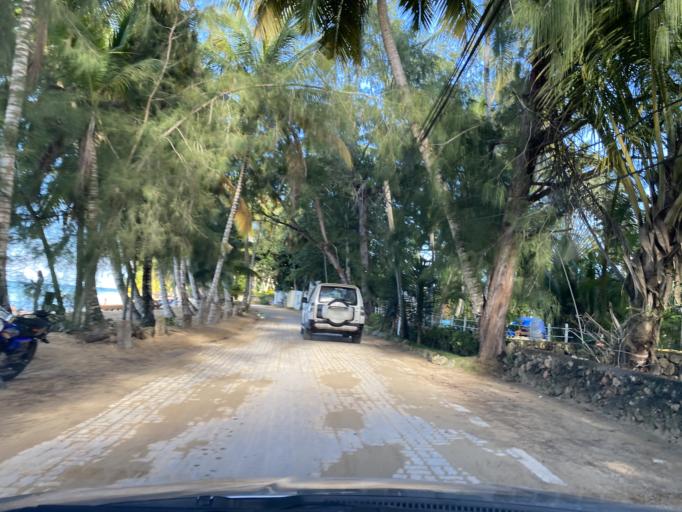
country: DO
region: Samana
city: Las Terrenas
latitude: 19.3227
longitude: -69.5540
